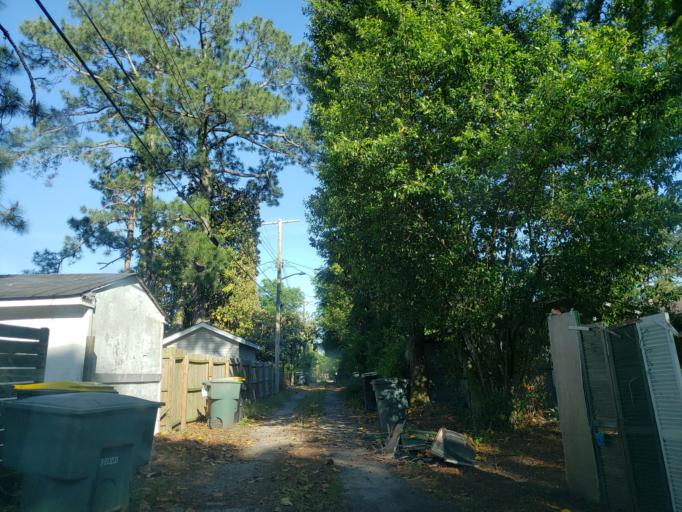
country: US
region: Georgia
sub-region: Chatham County
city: Thunderbolt
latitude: 32.0683
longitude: -81.0548
